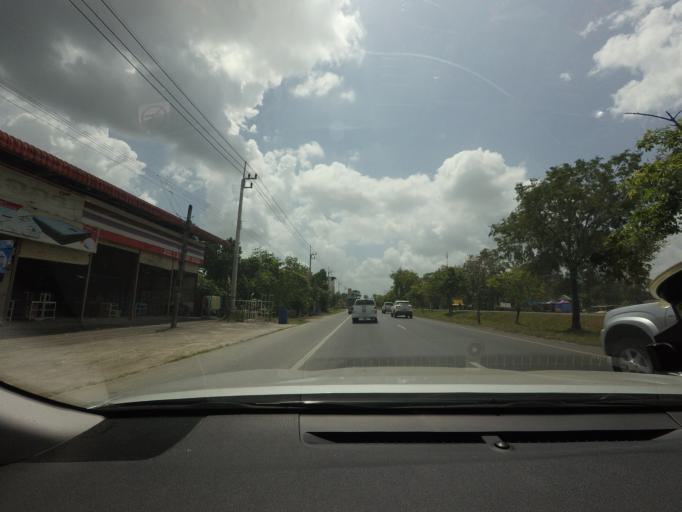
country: TH
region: Nakhon Si Thammarat
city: Nakhon Si Thammarat
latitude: 8.4212
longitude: 99.9214
